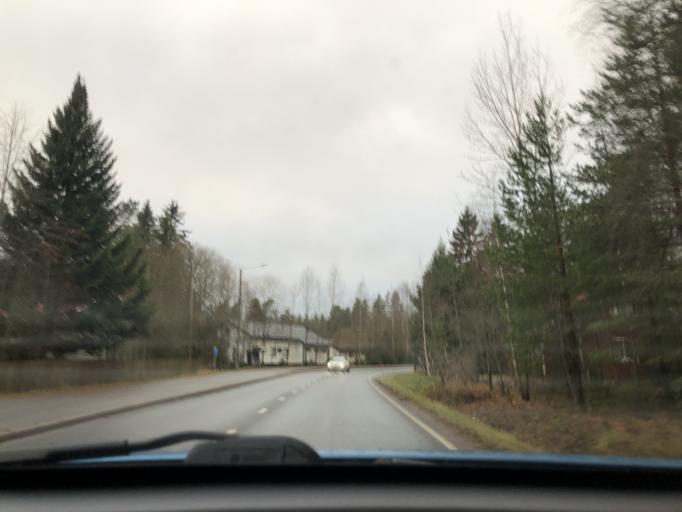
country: FI
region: Pirkanmaa
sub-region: Tampere
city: Kangasala
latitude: 61.5295
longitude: 24.0070
